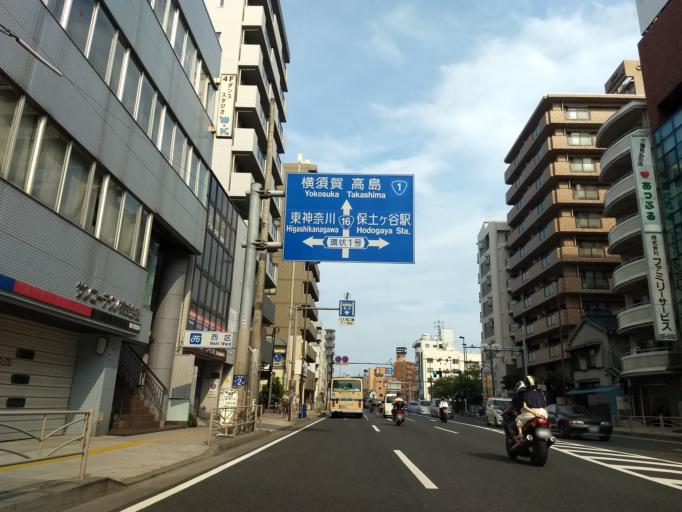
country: JP
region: Kanagawa
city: Yokohama
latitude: 35.4571
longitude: 139.6053
